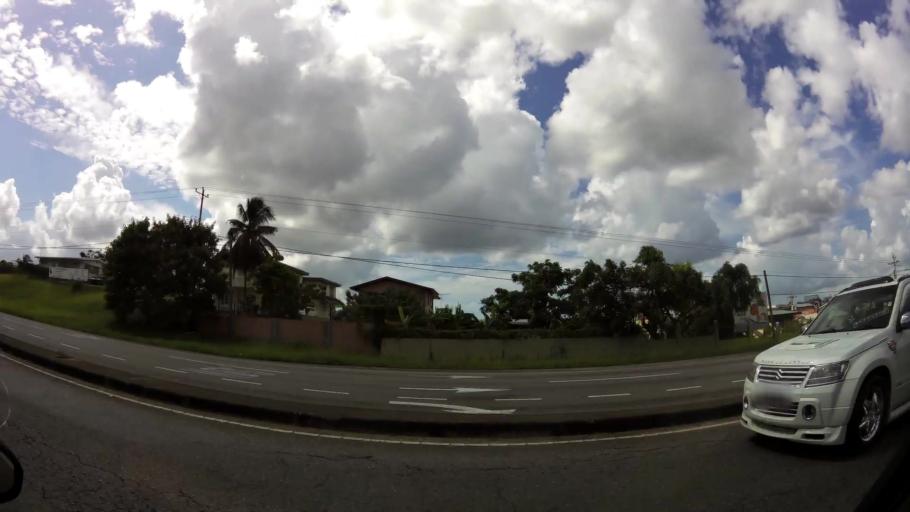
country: TT
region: City of San Fernando
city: Mon Repos
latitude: 10.2672
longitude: -61.4565
